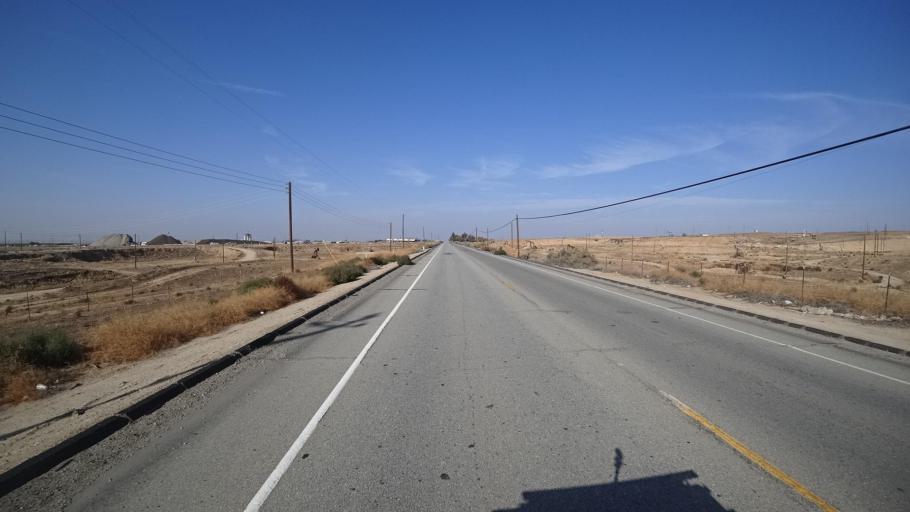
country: US
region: California
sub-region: Kern County
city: Oildale
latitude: 35.4663
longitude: -119.0597
